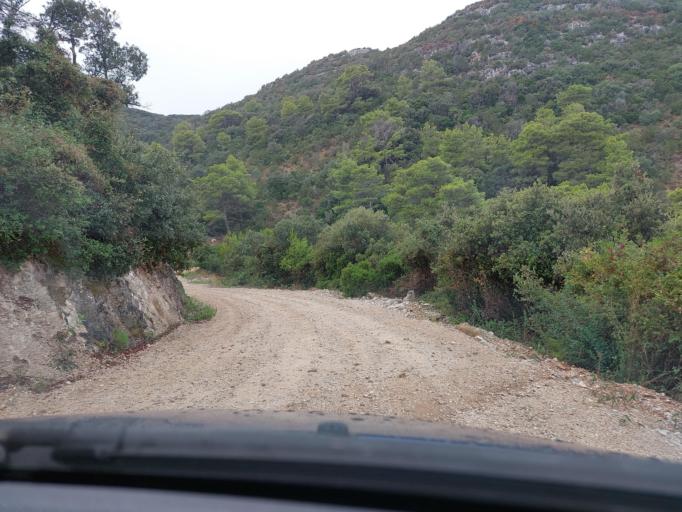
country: HR
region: Dubrovacko-Neretvanska
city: Smokvica
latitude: 42.7490
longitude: 16.9133
